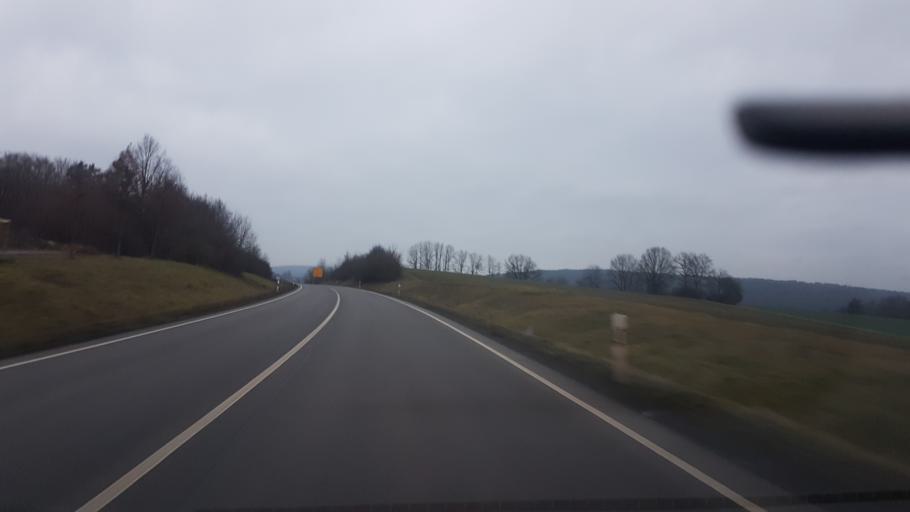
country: DE
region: Bavaria
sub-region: Upper Franconia
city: Reckendorf
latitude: 50.0286
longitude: 10.8269
